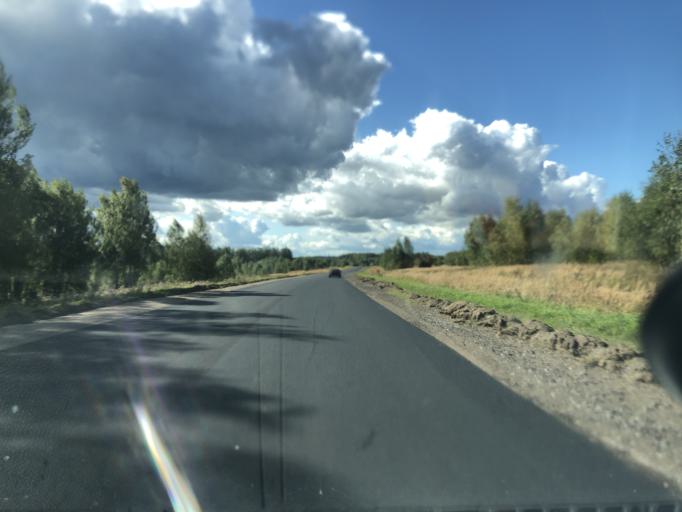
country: RU
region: Jaroslavl
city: Petrovsk
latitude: 56.9566
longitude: 39.3504
